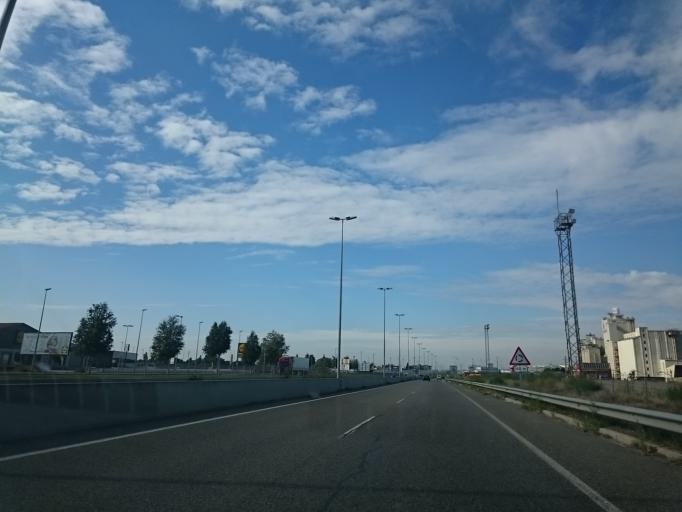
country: ES
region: Catalonia
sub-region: Provincia de Lleida
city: Lleida
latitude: 41.6159
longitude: 0.6562
